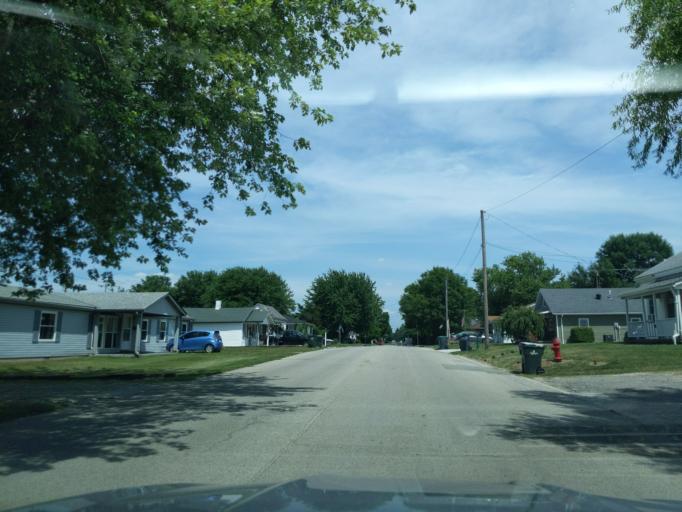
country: US
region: Indiana
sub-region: Decatur County
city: Greensburg
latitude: 39.3472
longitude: -85.4875
